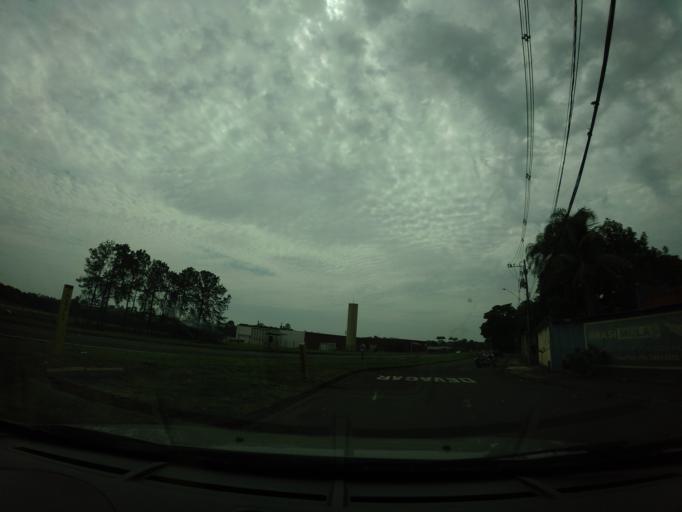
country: BR
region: Sao Paulo
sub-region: Piracicaba
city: Piracicaba
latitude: -22.7379
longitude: -47.5950
